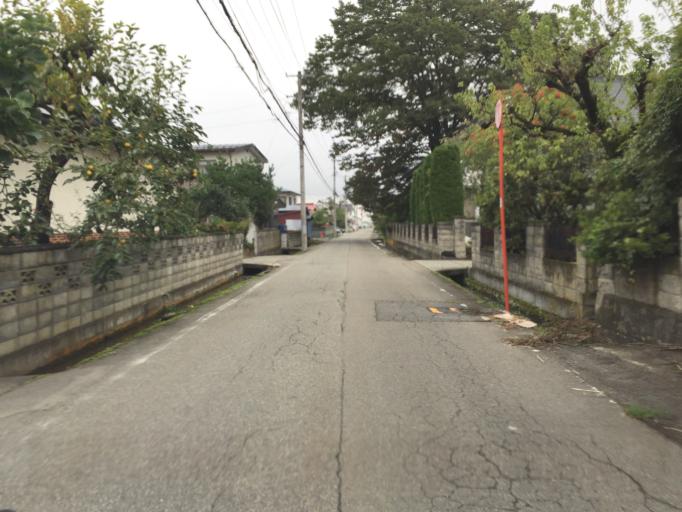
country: JP
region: Fukushima
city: Kitakata
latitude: 37.4581
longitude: 139.9153
